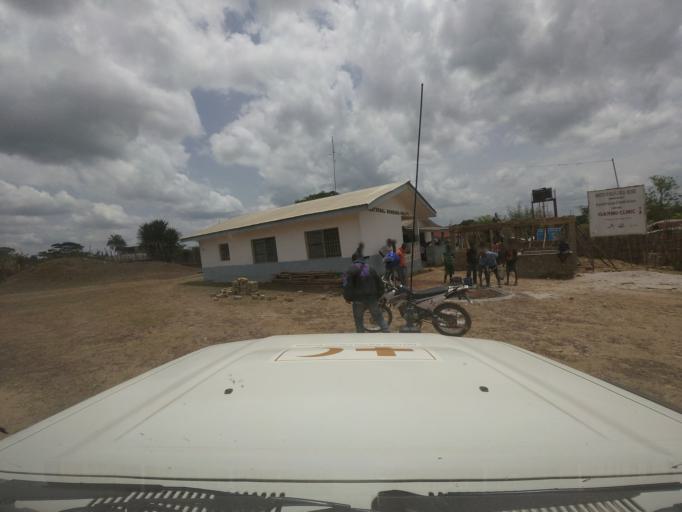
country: GN
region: Nzerekore
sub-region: Yomou
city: Yomou
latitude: 7.2335
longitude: -9.1665
